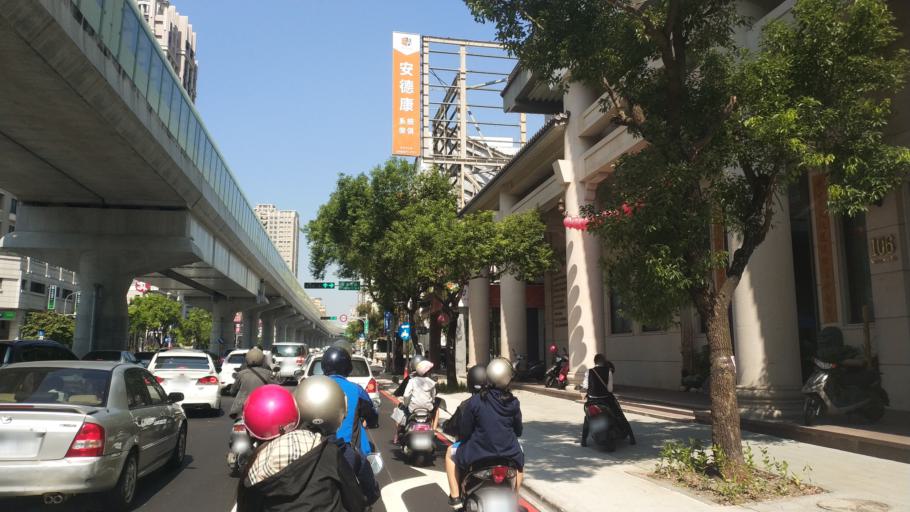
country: TW
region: Taiwan
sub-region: Taichung City
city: Taichung
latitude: 24.1340
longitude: 120.6466
